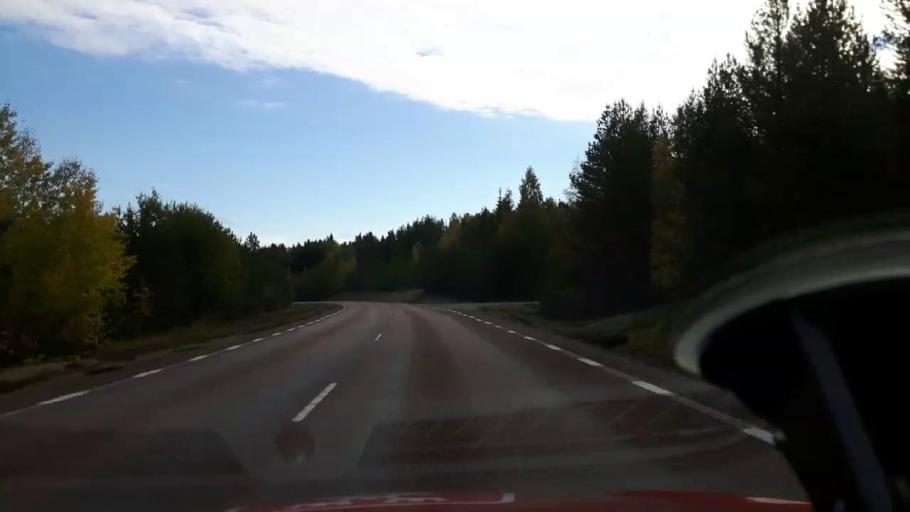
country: SE
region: Gaevleborg
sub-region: Ljusdals Kommun
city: Farila
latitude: 61.9364
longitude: 15.3998
